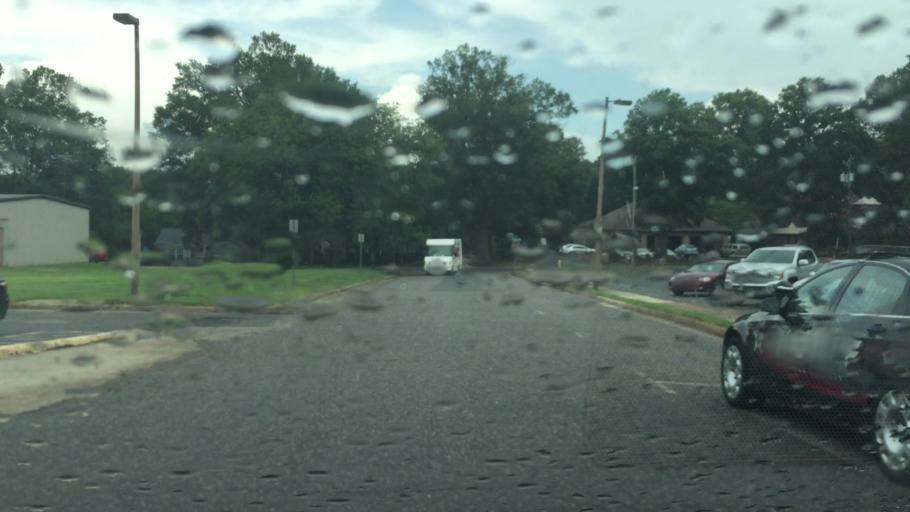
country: US
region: North Carolina
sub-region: Iredell County
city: Mooresville
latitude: 35.5803
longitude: -80.8031
